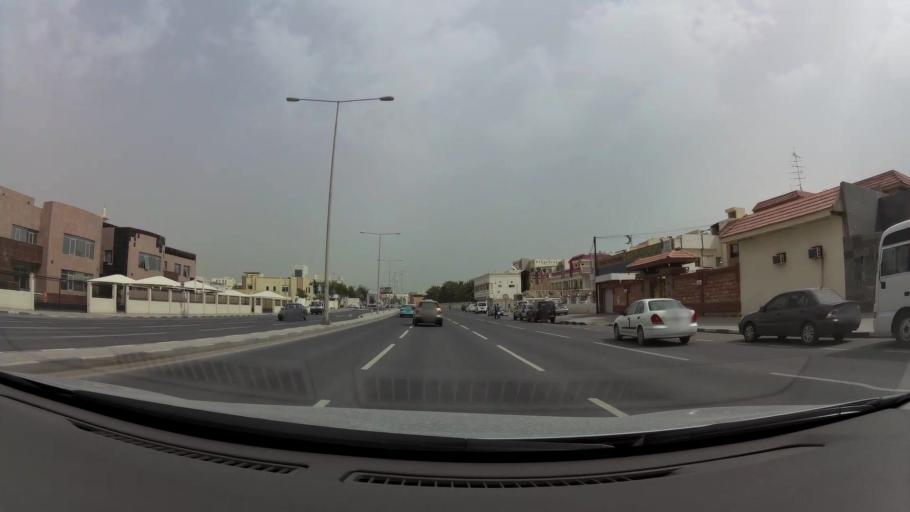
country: QA
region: Baladiyat ad Dawhah
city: Doha
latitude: 25.2597
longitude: 51.5375
